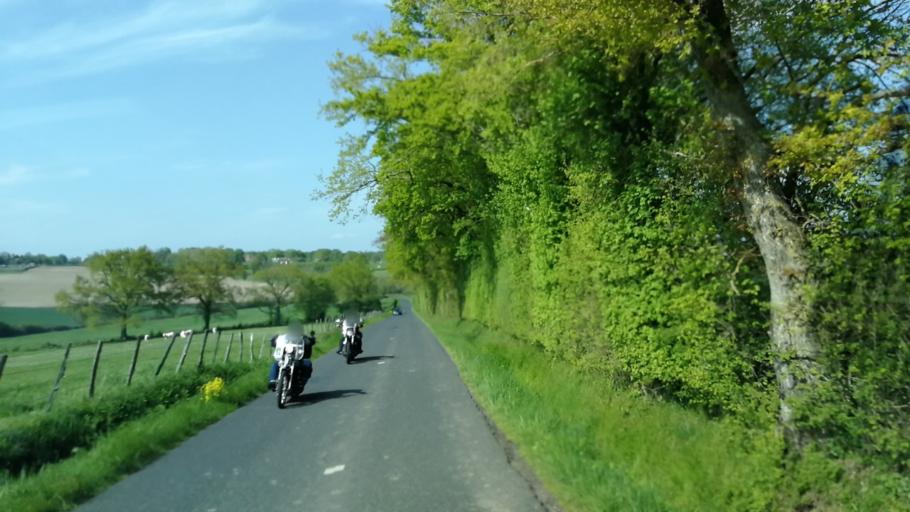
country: FR
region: Auvergne
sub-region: Departement de l'Allier
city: Saint-Gerand-le-Puy
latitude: 46.3968
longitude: 3.5799
